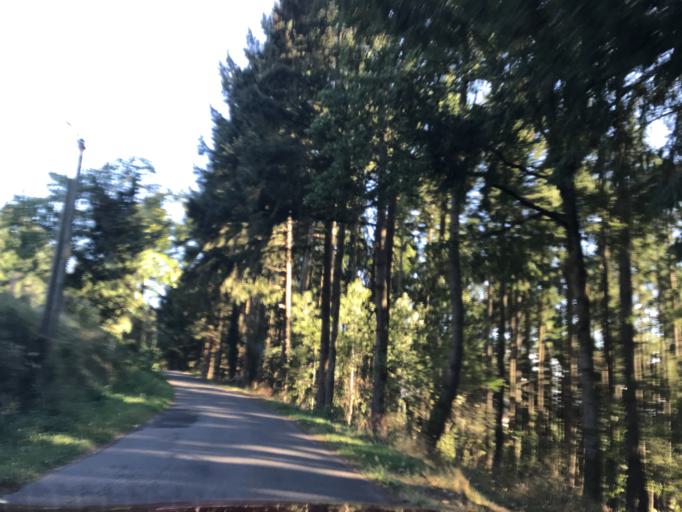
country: FR
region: Auvergne
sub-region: Departement du Puy-de-Dome
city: Escoutoux
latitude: 45.7788
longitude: 3.6065
